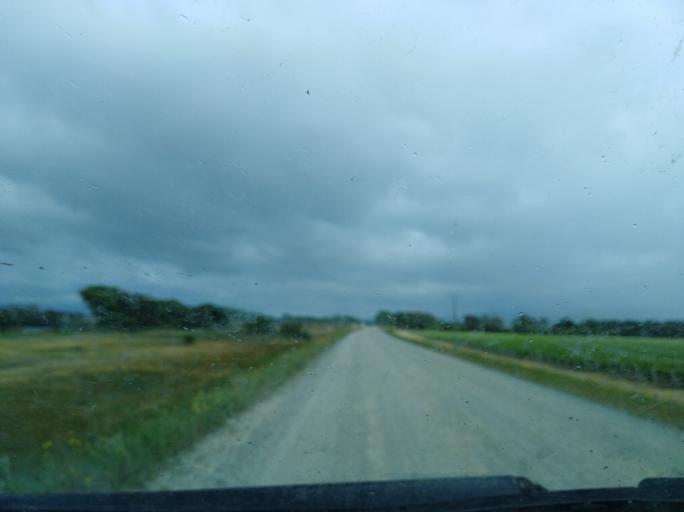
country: NZ
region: Marlborough
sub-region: Marlborough District
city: Blenheim
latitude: -41.4408
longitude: 174.0095
